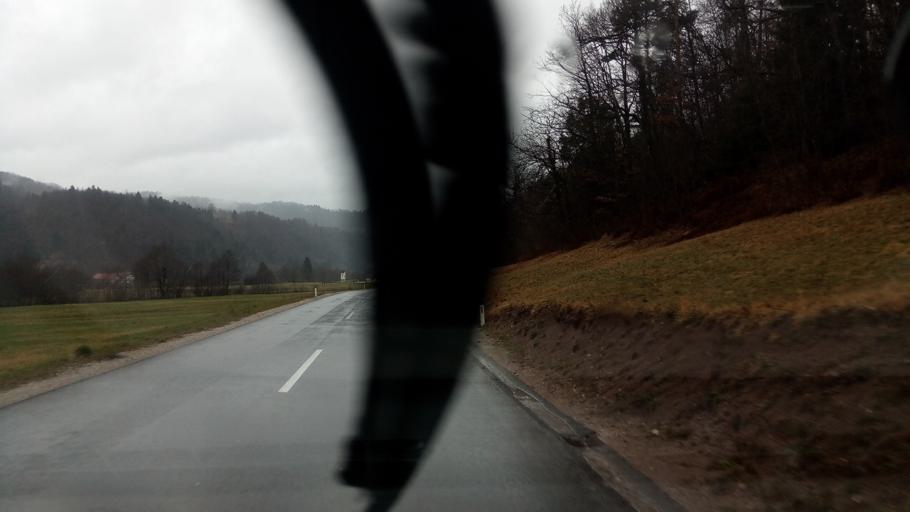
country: SI
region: Vrhnika
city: Vrhnika
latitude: 45.9953
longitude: 14.2460
